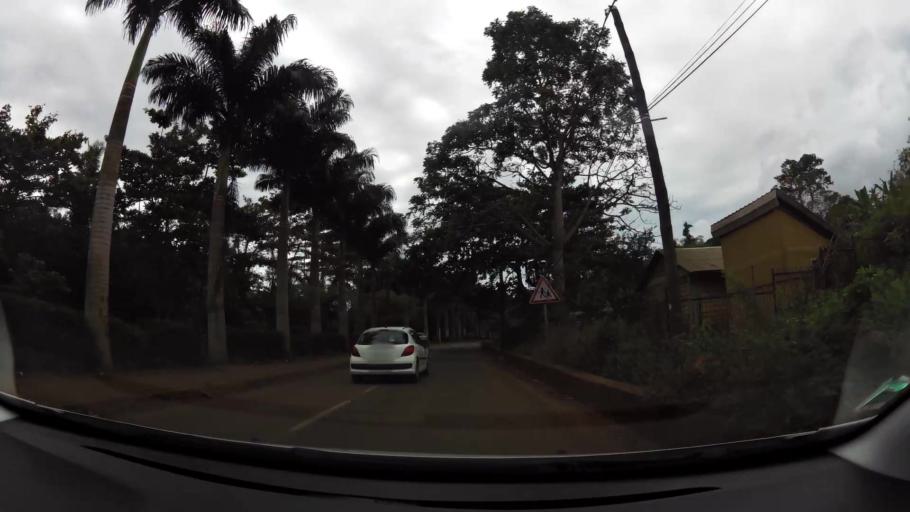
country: YT
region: Chiconi
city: Chiconi
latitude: -12.8327
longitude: 45.1168
